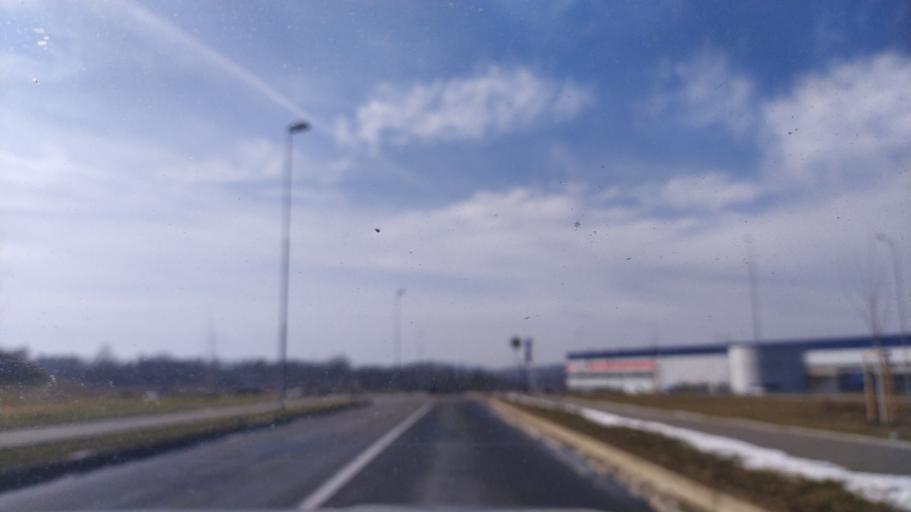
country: CZ
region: Karlovarsky
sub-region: Okres Cheb
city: Cheb
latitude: 50.0898
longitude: 12.4042
